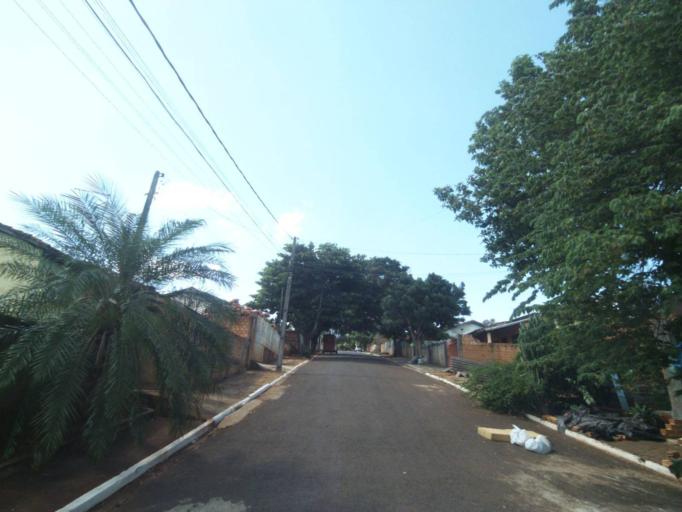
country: BR
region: Parana
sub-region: Sertanopolis
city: Sertanopolis
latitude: -23.0475
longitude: -50.8225
